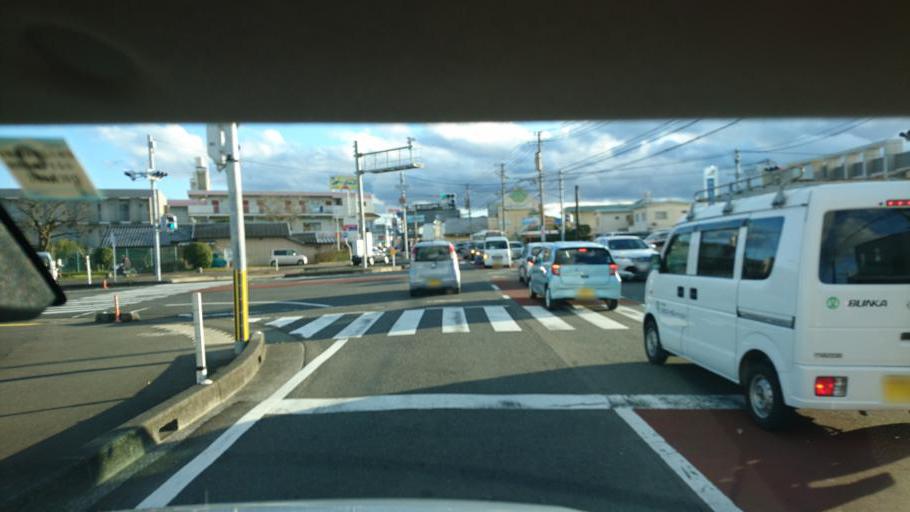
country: JP
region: Miyazaki
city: Miyazaki-shi
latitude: 31.8818
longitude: 131.4275
